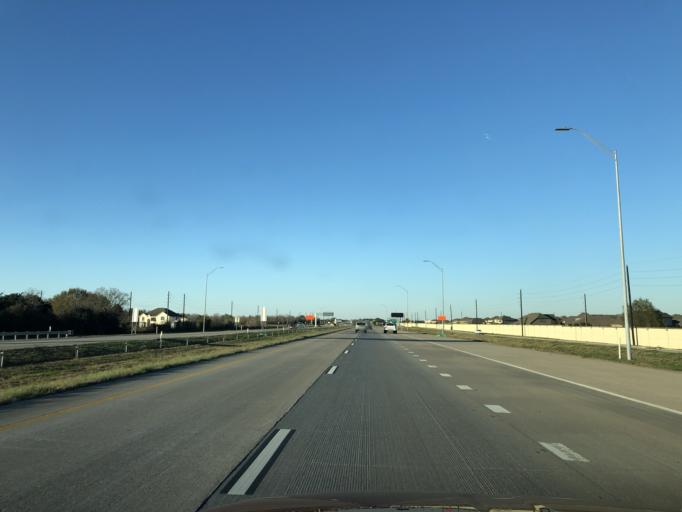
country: US
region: Texas
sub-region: Harris County
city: Cypress
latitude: 30.0058
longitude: -95.7689
